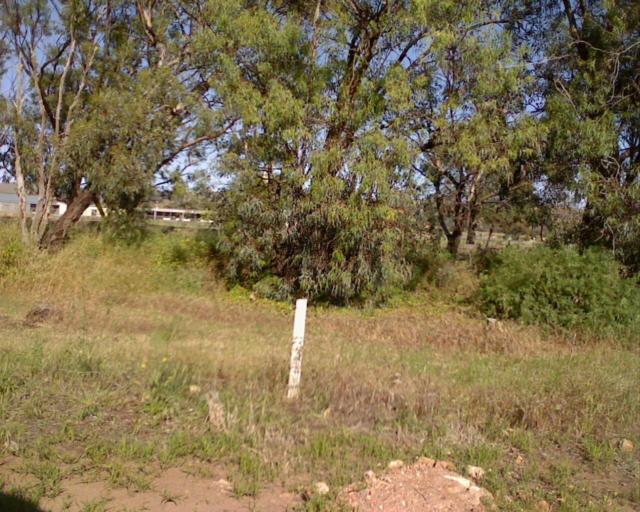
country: AU
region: South Australia
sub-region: Flinders Ranges
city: Quorn
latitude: -32.6490
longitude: 138.0955
